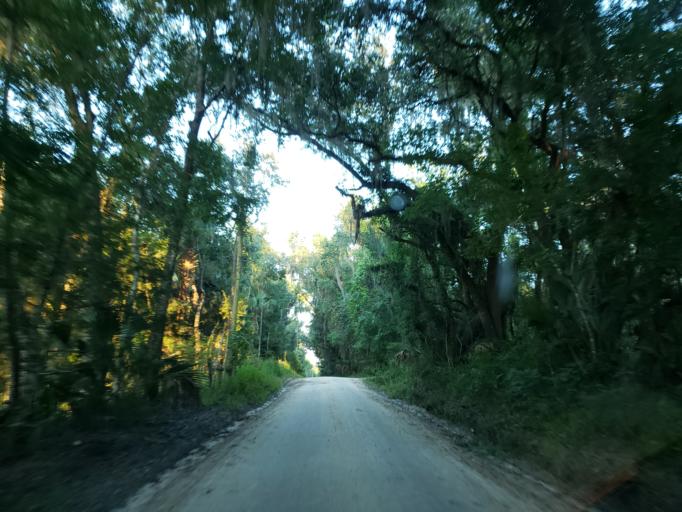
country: US
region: Florida
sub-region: Marion County
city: Citra
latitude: 29.4843
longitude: -82.2507
